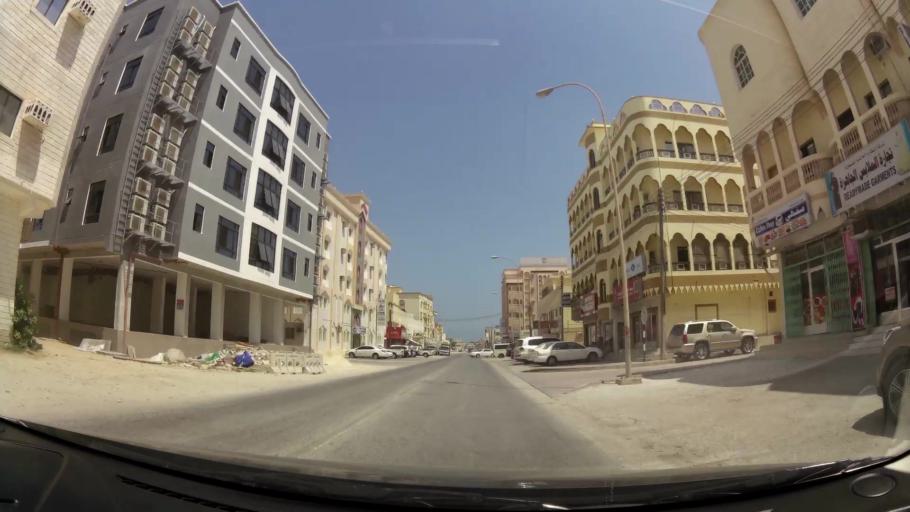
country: OM
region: Zufar
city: Salalah
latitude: 17.0158
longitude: 54.0806
